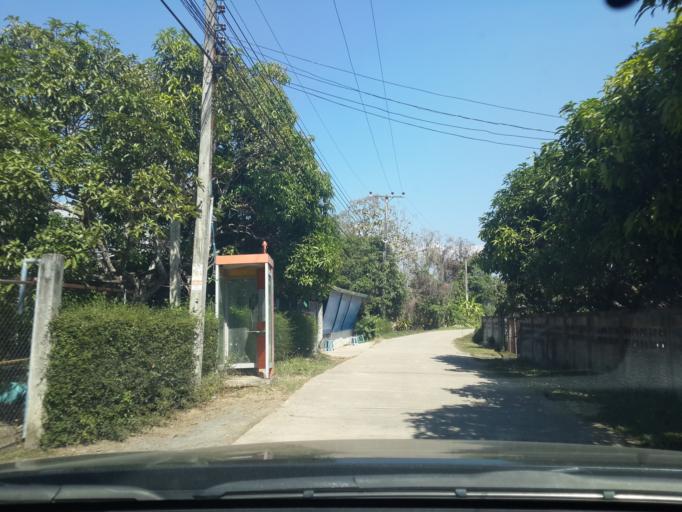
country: TH
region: Chiang Mai
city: San Sai
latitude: 18.8823
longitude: 99.1112
